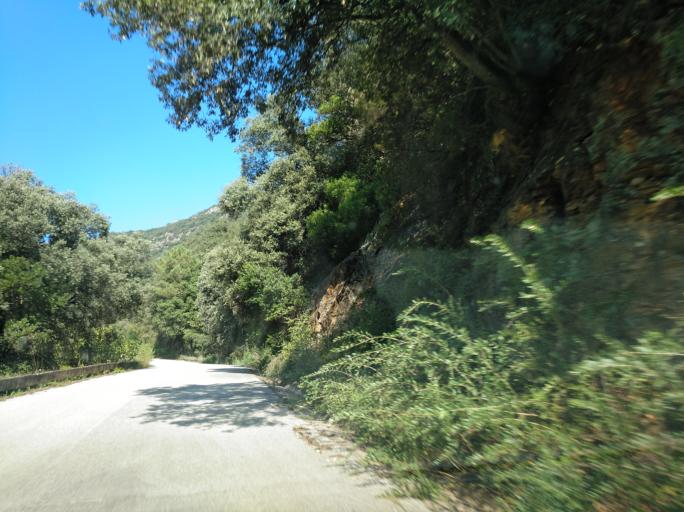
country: ES
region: Catalonia
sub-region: Provincia de Girona
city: Susqueda
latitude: 41.9853
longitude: 2.5362
